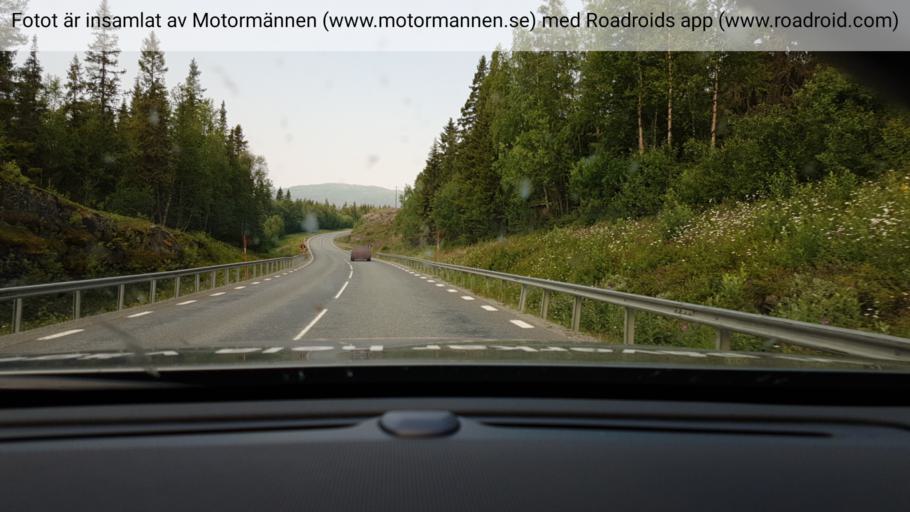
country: SE
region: Vaesterbotten
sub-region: Vilhelmina Kommun
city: Sjoberg
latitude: 65.5508
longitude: 15.5650
